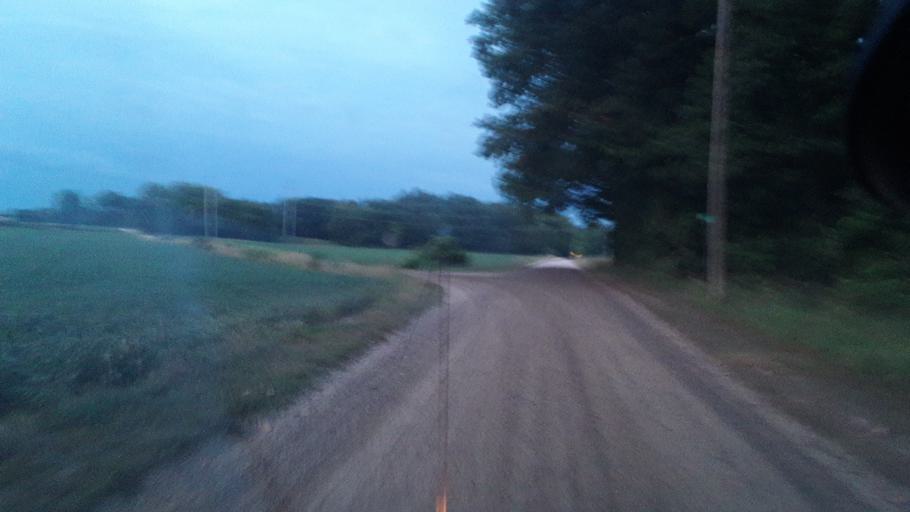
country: US
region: Indiana
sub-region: DeKalb County
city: Butler
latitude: 41.3539
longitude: -84.8303
